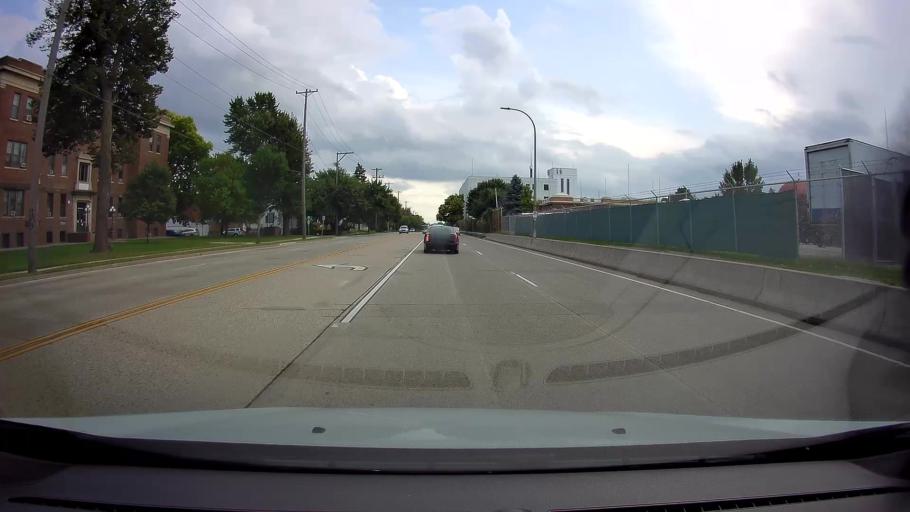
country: US
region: Minnesota
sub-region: Ramsey County
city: Falcon Heights
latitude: 44.9854
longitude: -93.1670
